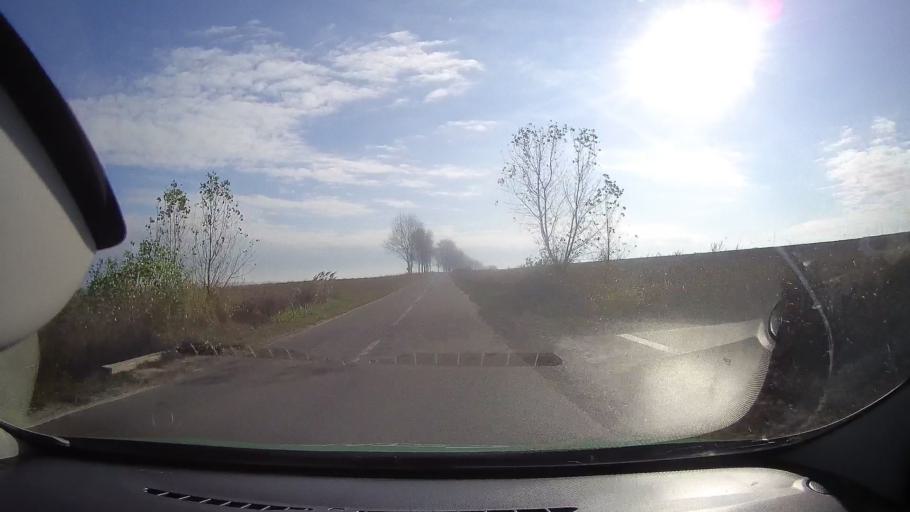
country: RO
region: Tulcea
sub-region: Comuna Mahmudia
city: Mahmudia
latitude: 45.0676
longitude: 29.1037
